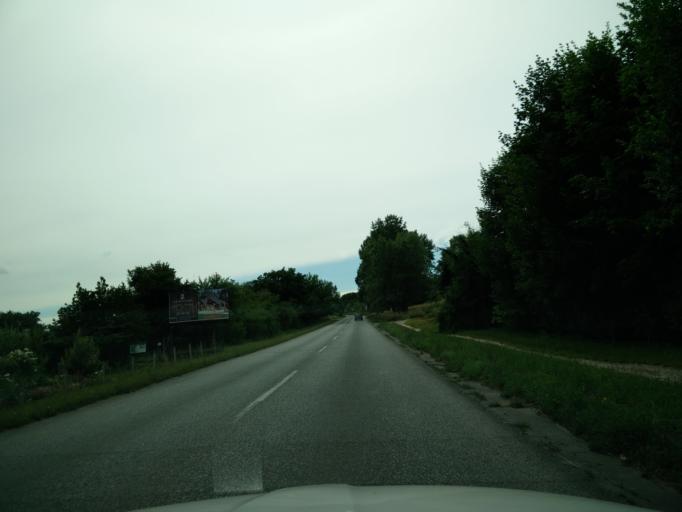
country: SK
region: Nitriansky
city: Bojnice
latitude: 48.7747
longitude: 18.5848
